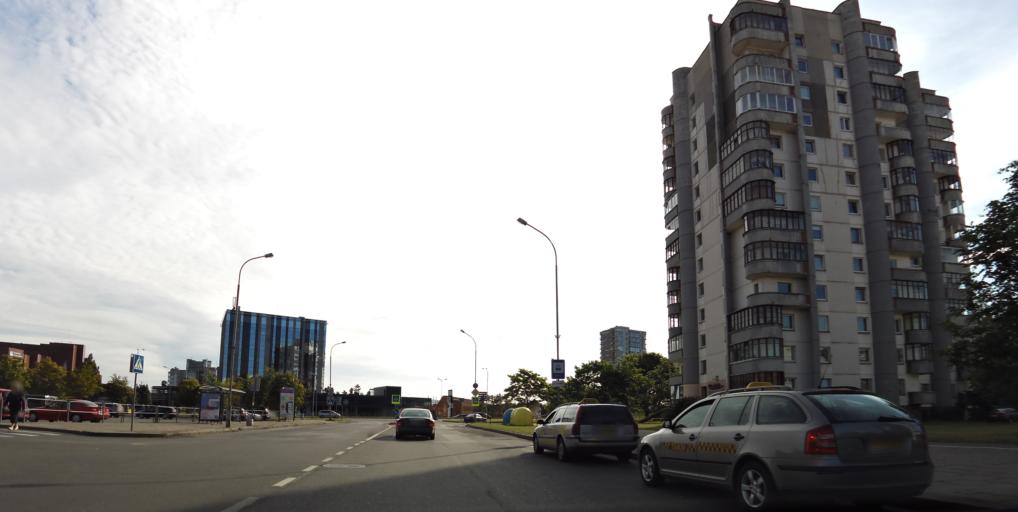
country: LT
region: Vilnius County
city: Seskine
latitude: 54.7149
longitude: 25.2458
